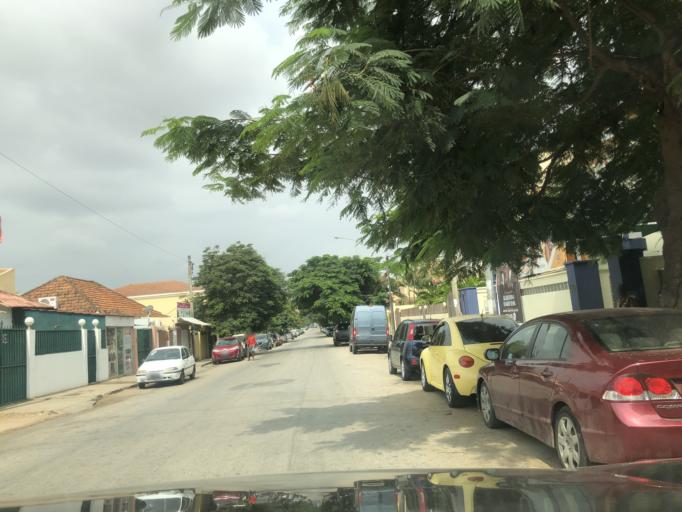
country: AO
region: Luanda
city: Luanda
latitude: -8.8304
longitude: 13.2508
